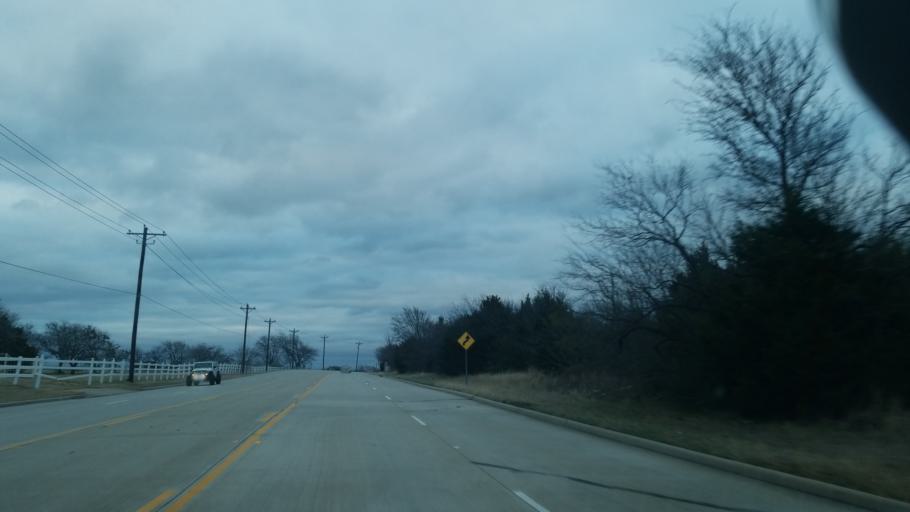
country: US
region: Texas
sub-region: Denton County
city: Little Elm
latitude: 33.1429
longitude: -96.9814
